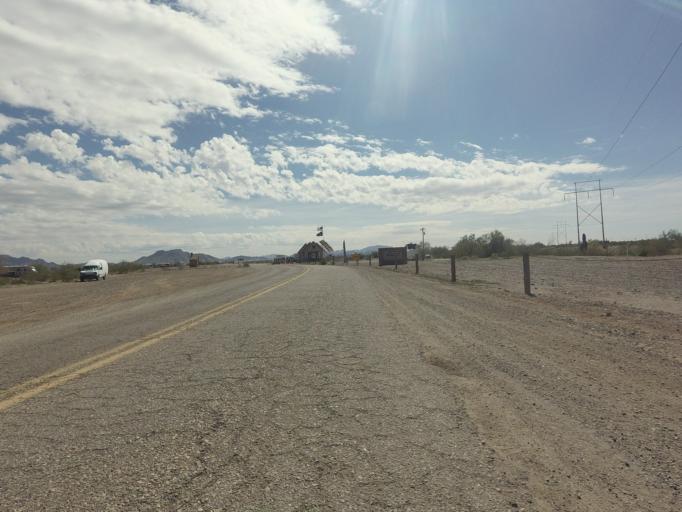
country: US
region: Arizona
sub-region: La Paz County
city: Quartzsite
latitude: 33.6261
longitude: -114.2166
